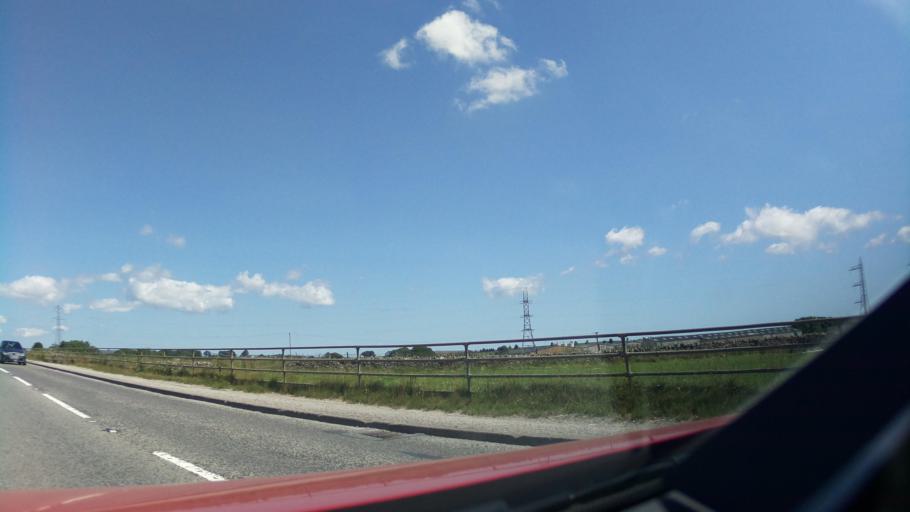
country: GB
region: England
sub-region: Derbyshire
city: Buxton
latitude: 53.2755
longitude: -1.8920
